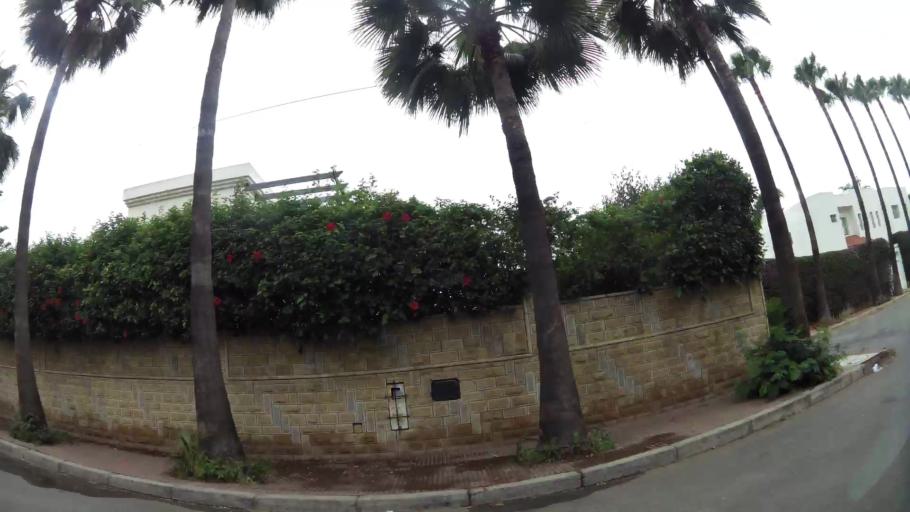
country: MA
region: Rabat-Sale-Zemmour-Zaer
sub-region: Rabat
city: Rabat
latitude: 33.9725
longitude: -6.8231
